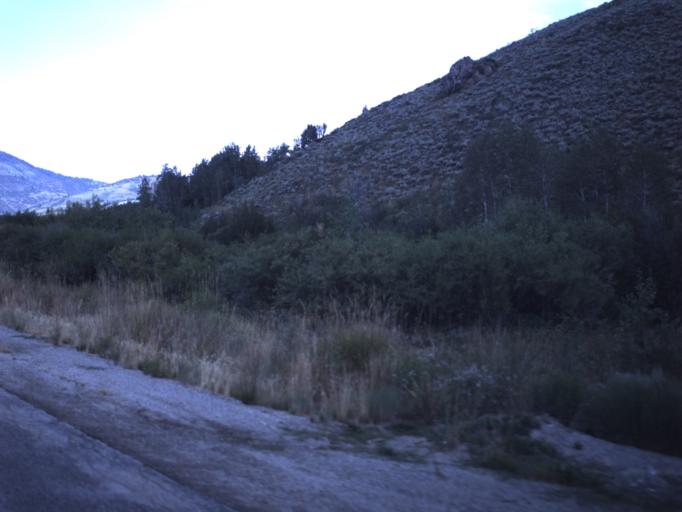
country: US
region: Utah
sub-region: Cache County
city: Richmond
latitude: 41.8891
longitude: -111.5652
